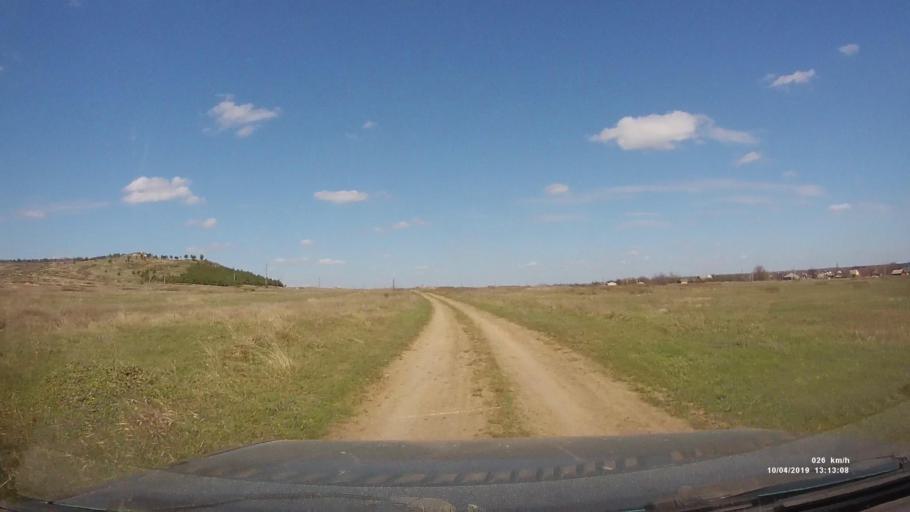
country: RU
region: Rostov
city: Masalovka
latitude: 48.4156
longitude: 40.2582
